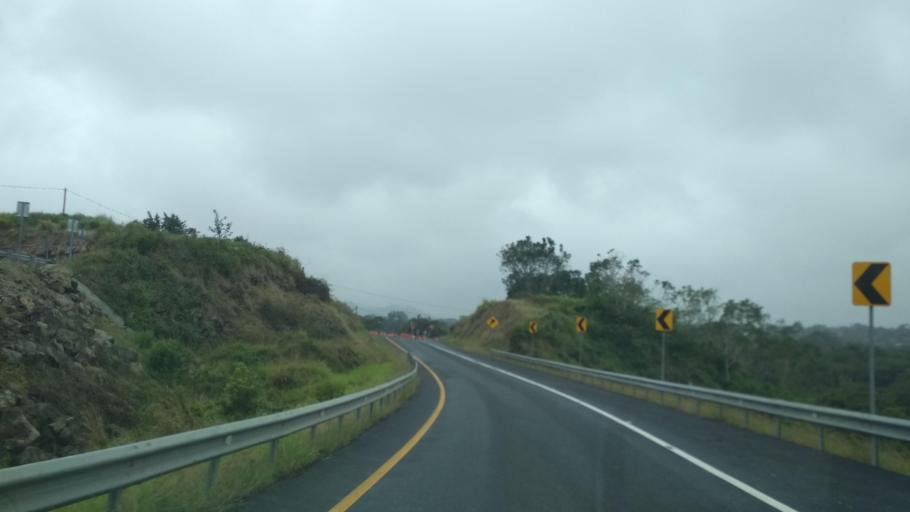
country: MX
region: Veracruz
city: Vega de San Marcos
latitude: 20.1480
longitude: -96.9481
